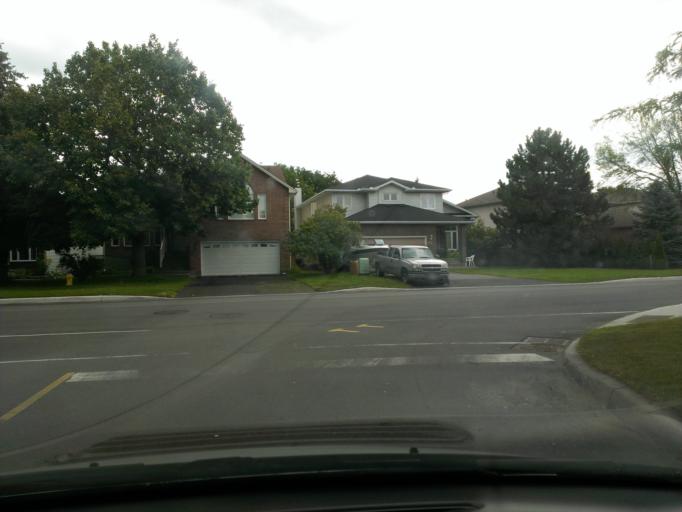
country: CA
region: Quebec
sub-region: Outaouais
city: Gatineau
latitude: 45.4815
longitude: -75.4968
